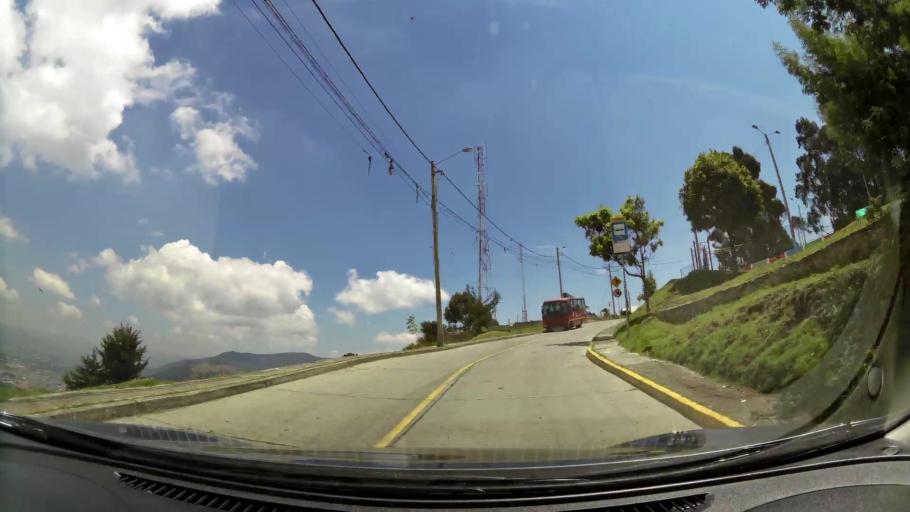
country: CO
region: Cundinamarca
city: La Calera
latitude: 4.7292
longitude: -74.0152
